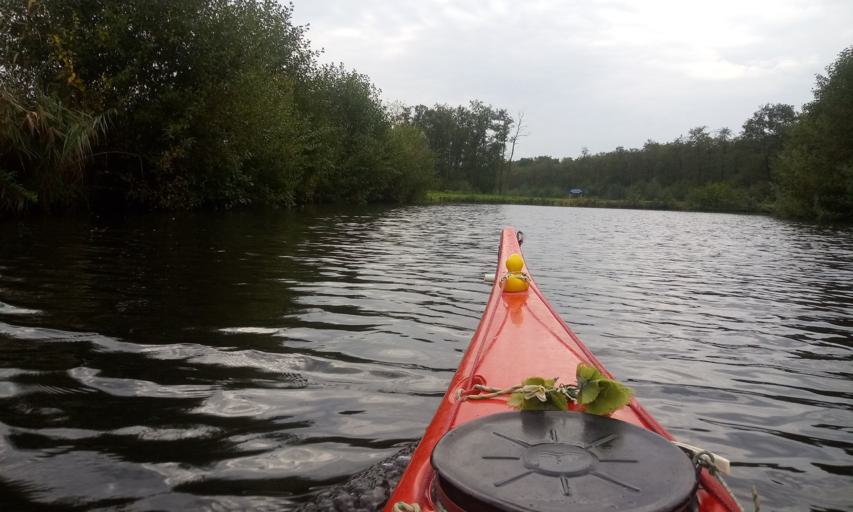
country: NL
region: North Holland
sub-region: Gemeente Wijdemeren
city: Oud-Loosdrecht
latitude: 52.2008
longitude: 5.1079
